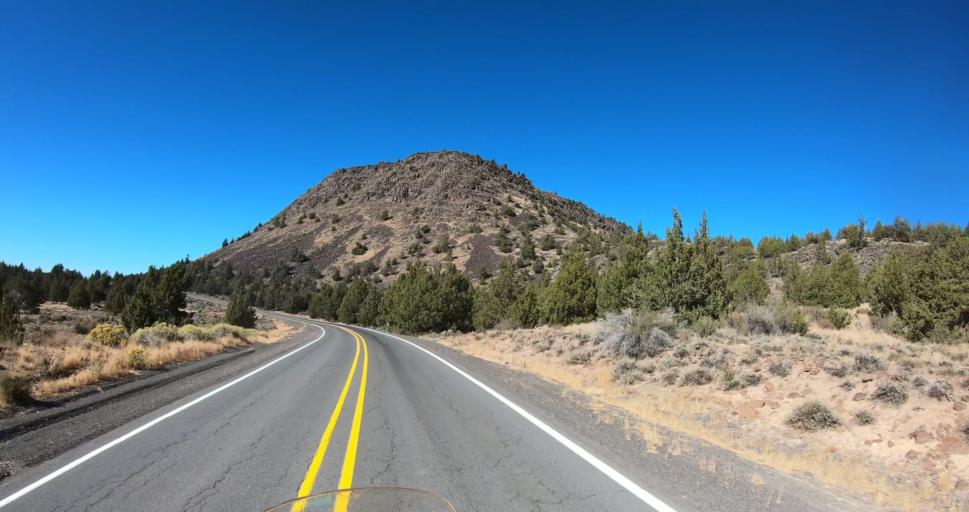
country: US
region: Oregon
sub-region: Deschutes County
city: La Pine
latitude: 43.0451
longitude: -120.7952
